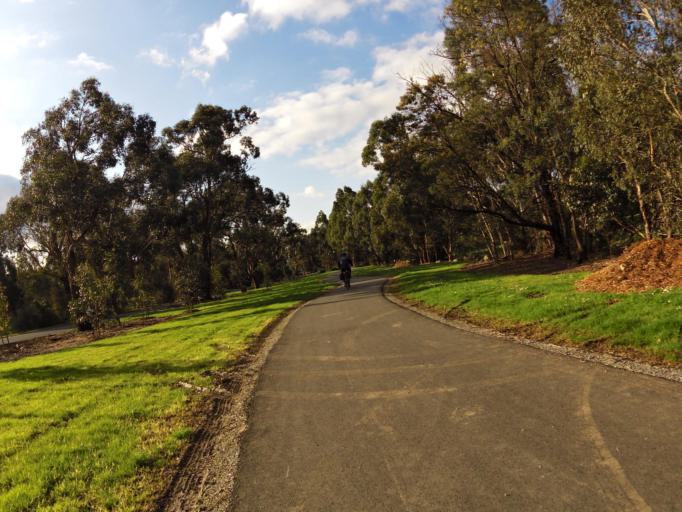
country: AU
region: Victoria
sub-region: Maroondah
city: Bayswater North
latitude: -37.8396
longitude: 145.3011
